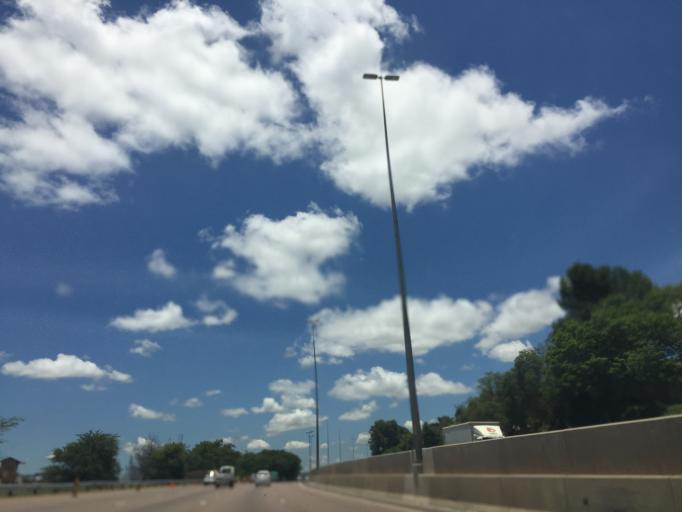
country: ZA
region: Gauteng
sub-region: City of Tshwane Metropolitan Municipality
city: Pretoria
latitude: -25.6952
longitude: 28.2822
